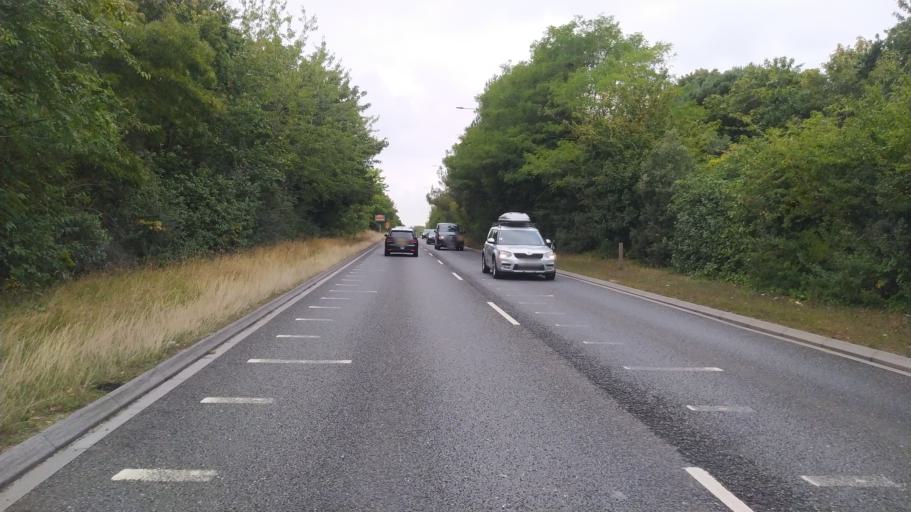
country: GB
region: England
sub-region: Bournemouth
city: Bournemouth
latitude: 50.7233
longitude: -1.8985
